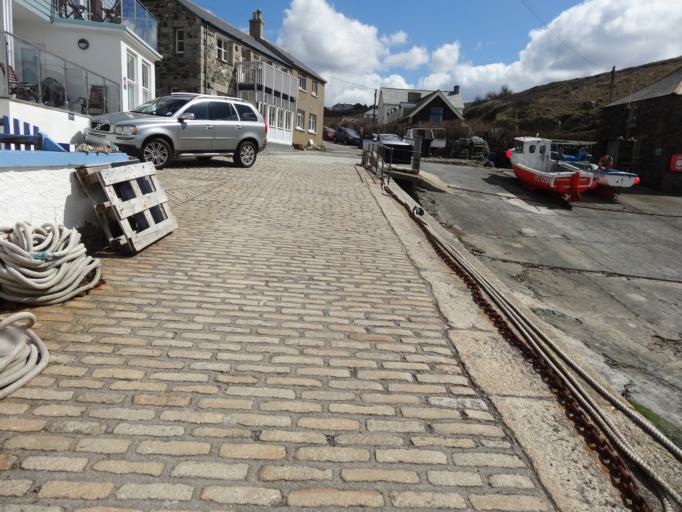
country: GB
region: England
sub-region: Cornwall
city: Mullion
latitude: 50.0155
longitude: -5.2579
